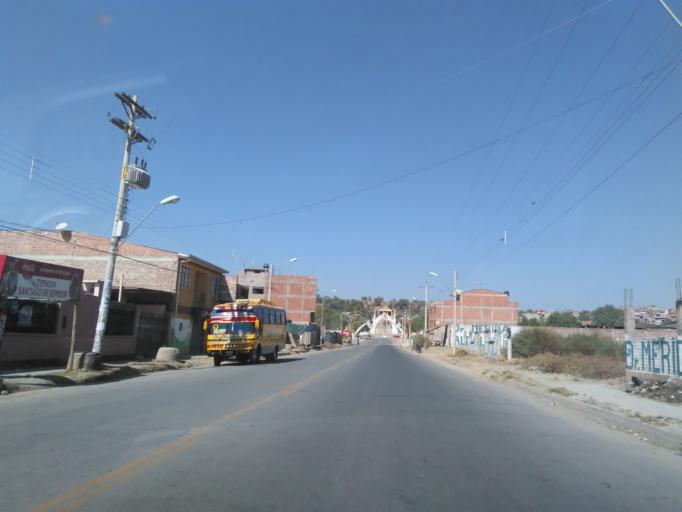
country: BO
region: Cochabamba
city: Sipe Sipe
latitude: -17.4170
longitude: -66.2833
